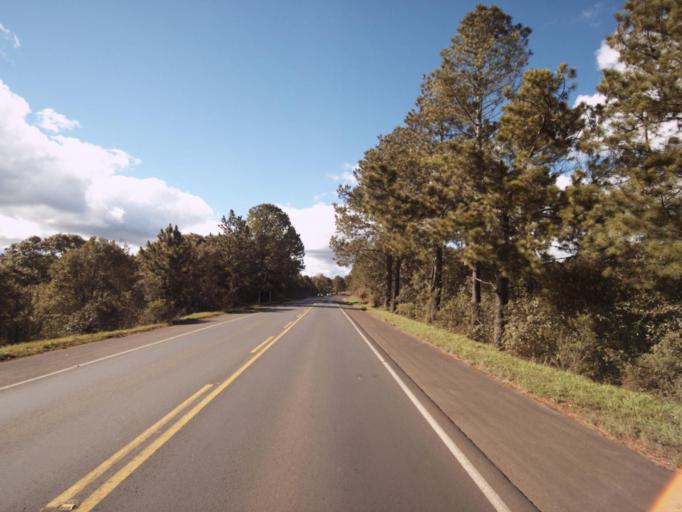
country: BR
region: Santa Catarina
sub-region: Joacaba
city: Joacaba
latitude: -26.9770
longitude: -51.7819
